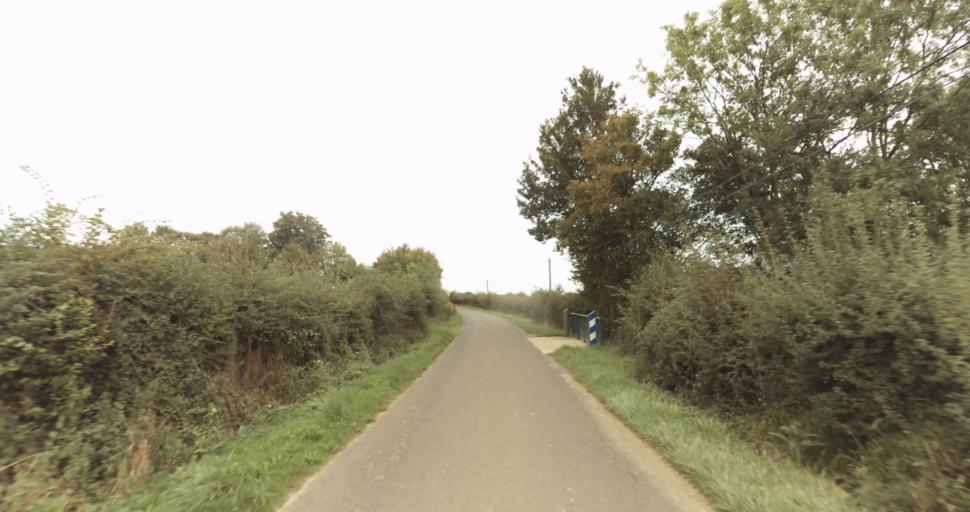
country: FR
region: Lower Normandy
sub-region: Departement de l'Orne
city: Gace
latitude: 48.7666
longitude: 0.3080
